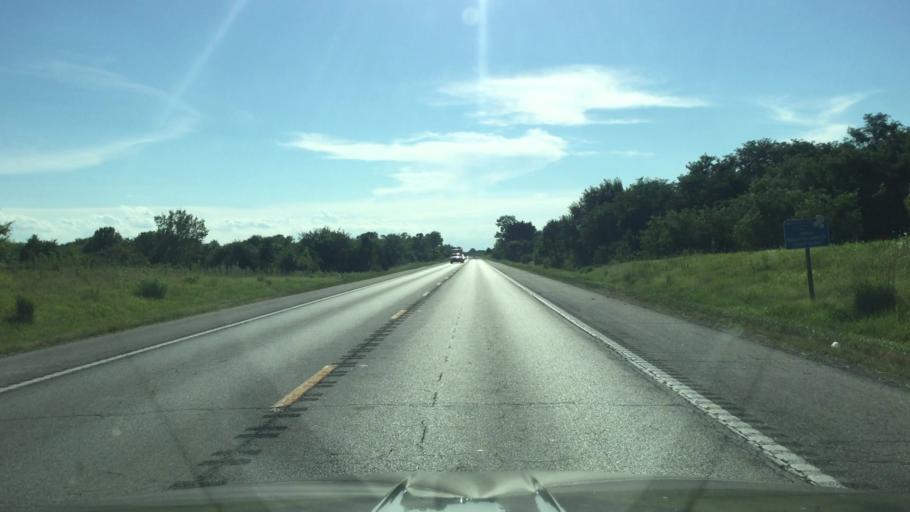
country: US
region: Missouri
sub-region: Pettis County
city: Sedalia
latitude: 38.6948
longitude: -93.1257
